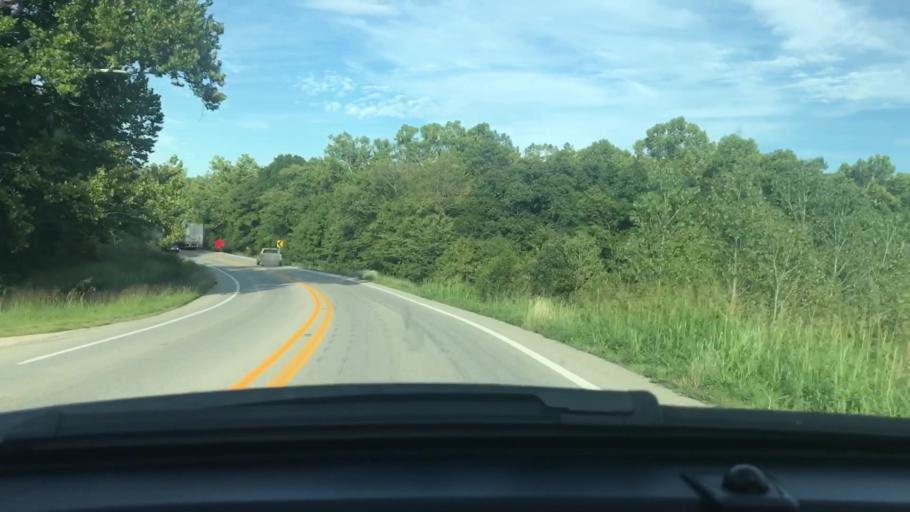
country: US
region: Arkansas
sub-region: Sharp County
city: Cherokee Village
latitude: 36.2973
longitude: -91.4343
